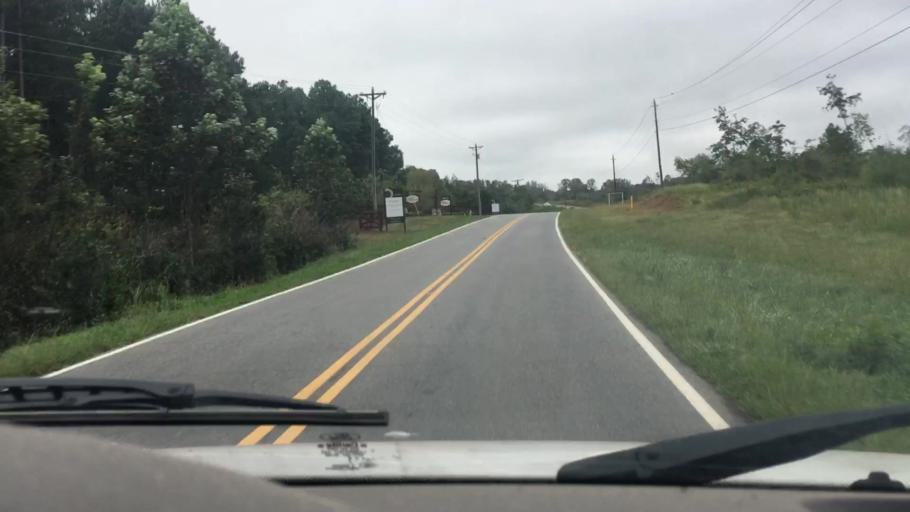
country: US
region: North Carolina
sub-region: Lincoln County
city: Denver
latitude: 35.5465
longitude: -81.0054
